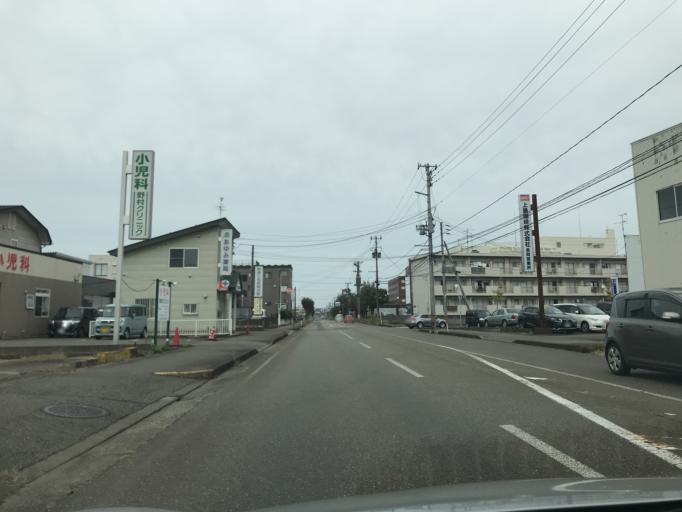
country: JP
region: Niigata
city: Nagaoka
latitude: 37.4334
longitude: 138.8376
